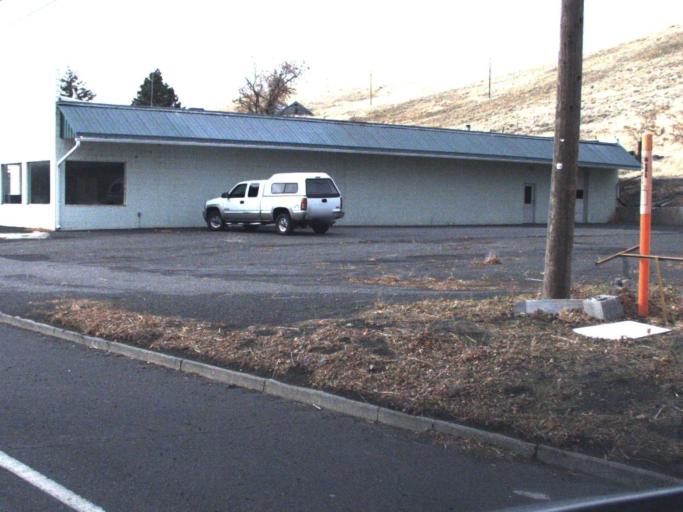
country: US
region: Washington
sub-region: Garfield County
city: Pomeroy
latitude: 46.4744
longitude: -117.5831
